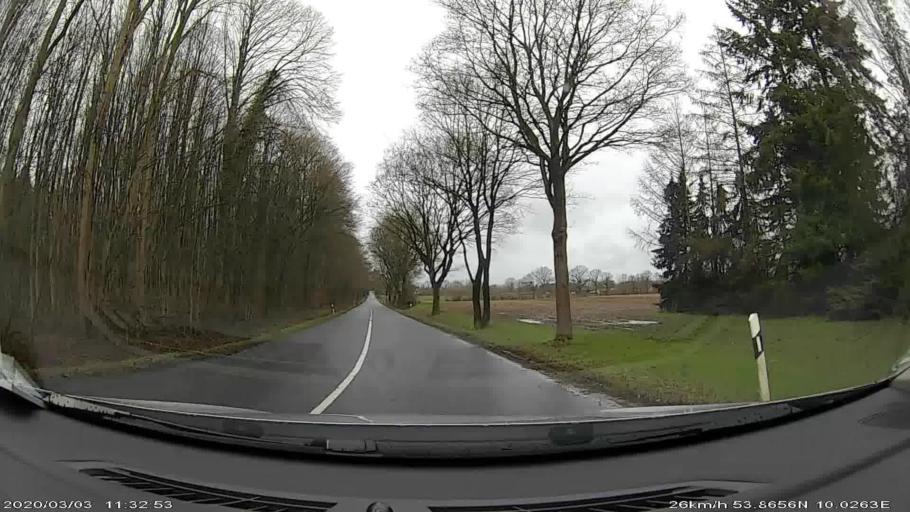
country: DE
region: Schleswig-Holstein
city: Kattendorf
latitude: 53.8665
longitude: 10.0228
